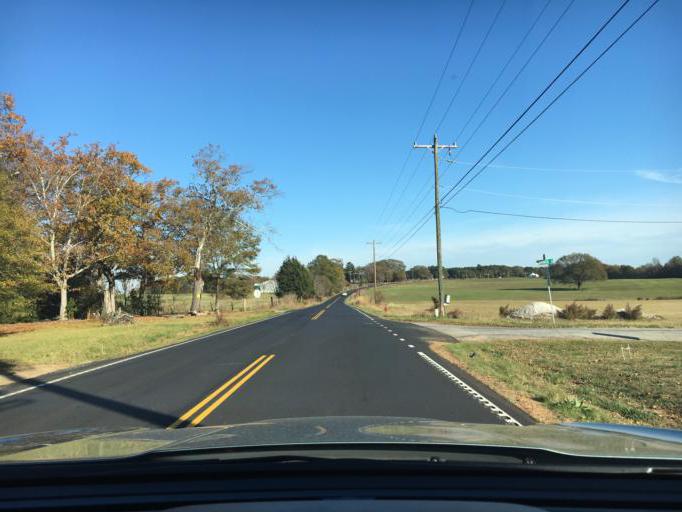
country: US
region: South Carolina
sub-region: Spartanburg County
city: Inman Mills
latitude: 35.0304
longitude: -82.1097
